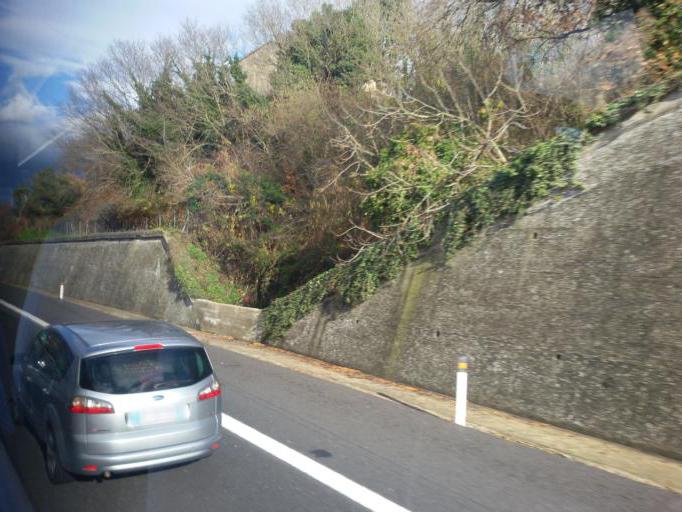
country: IT
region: Umbria
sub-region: Provincia di Terni
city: Baschi
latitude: 42.6816
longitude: 12.2114
